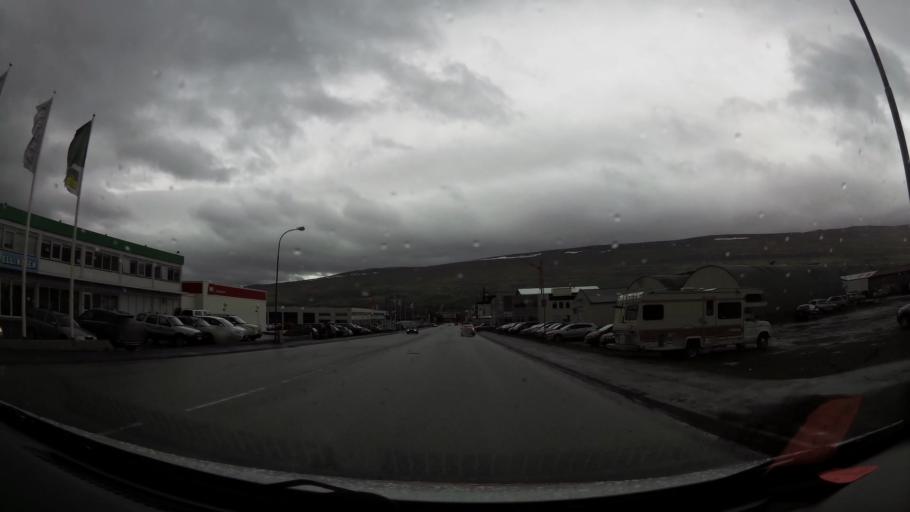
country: IS
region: Northeast
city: Akureyri
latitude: 65.6891
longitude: -18.1001
